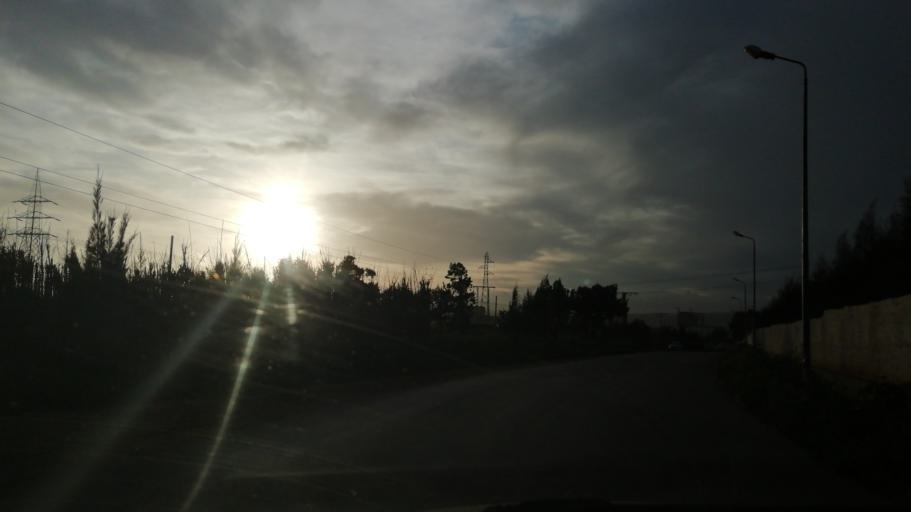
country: DZ
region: Oran
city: Es Senia
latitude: 35.6786
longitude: -0.5870
